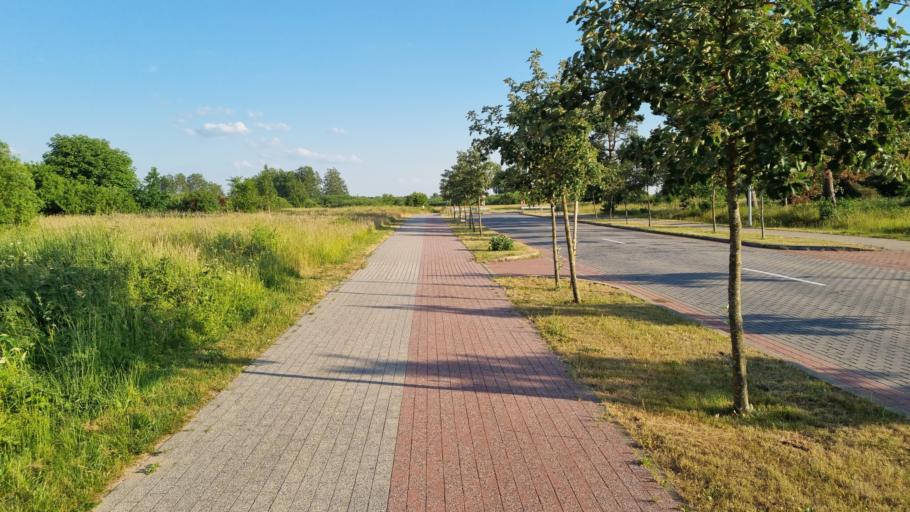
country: LV
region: Ventspils
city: Ventspils
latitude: 57.3755
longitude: 21.5962
